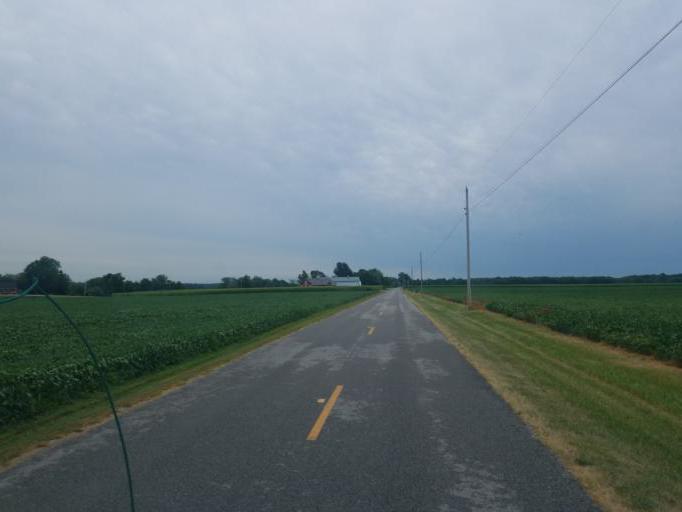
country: US
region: Ohio
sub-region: Paulding County
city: Antwerp
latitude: 41.2373
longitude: -84.7342
